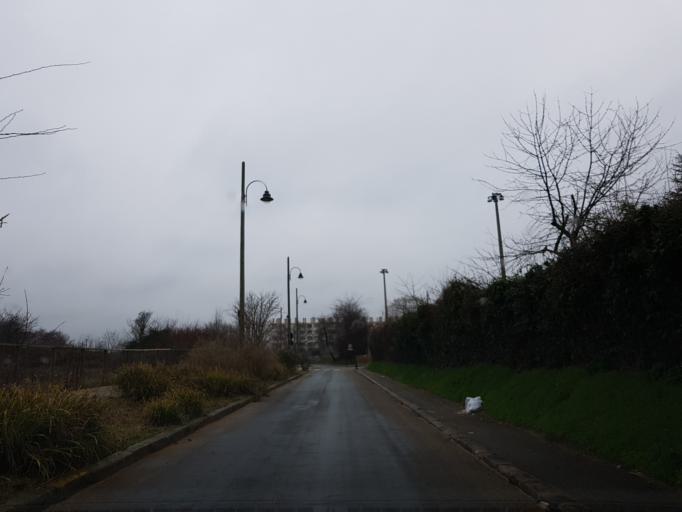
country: FR
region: Ile-de-France
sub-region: Departement du Val-de-Marne
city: Vitry-sur-Seine
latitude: 48.7820
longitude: 2.3852
